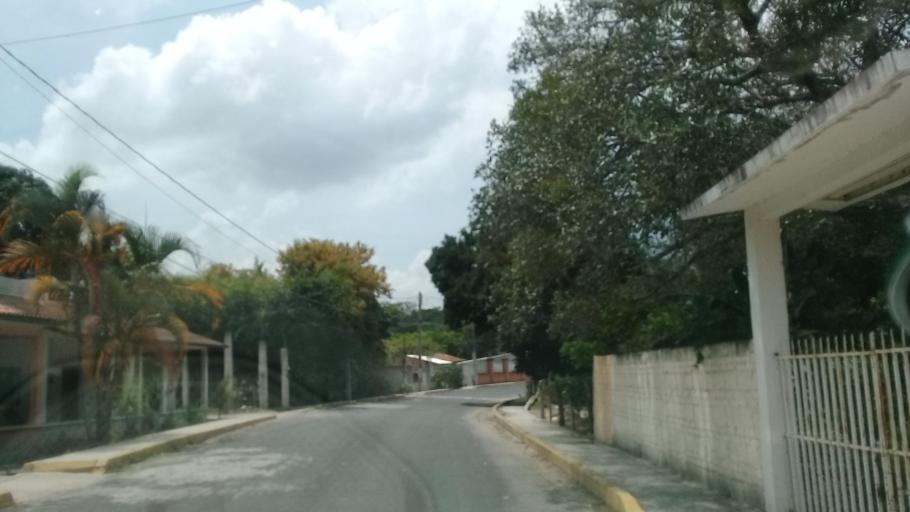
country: MX
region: Veracruz
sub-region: Emiliano Zapata
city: Plan del Rio
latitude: 19.4302
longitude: -96.6983
